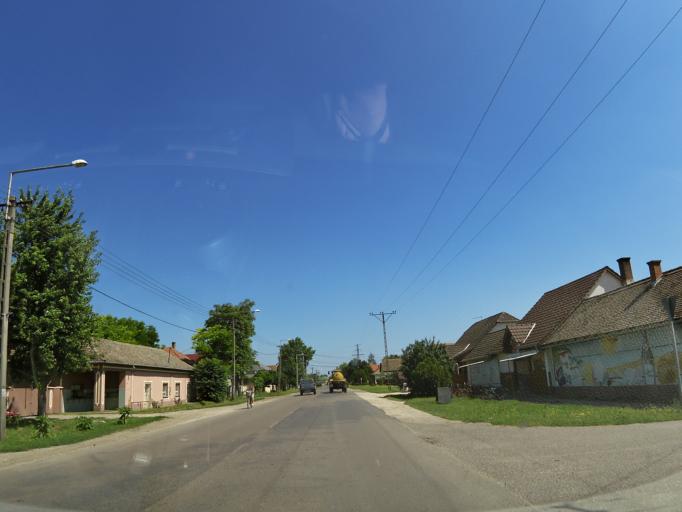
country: HU
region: Jasz-Nagykun-Szolnok
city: Kunhegyes
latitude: 47.3593
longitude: 20.6250
